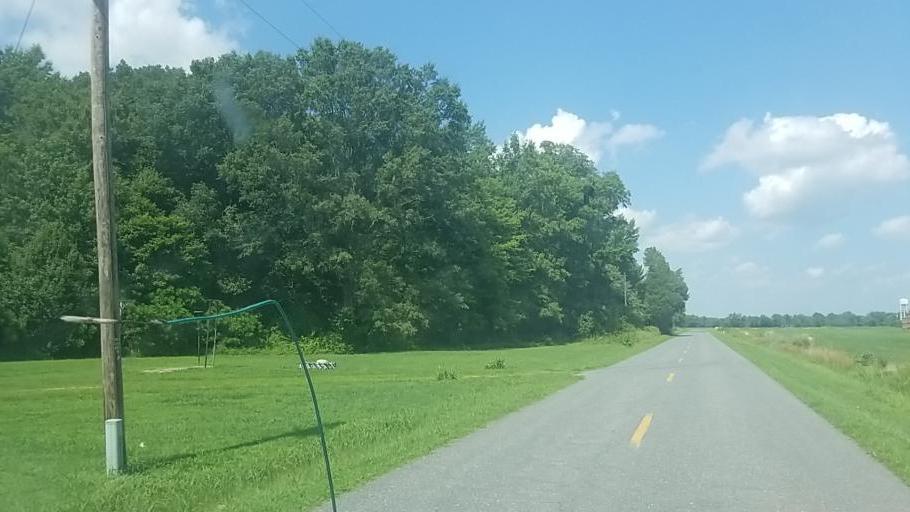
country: US
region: Maryland
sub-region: Dorchester County
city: Hurlock
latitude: 38.4758
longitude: -75.8393
